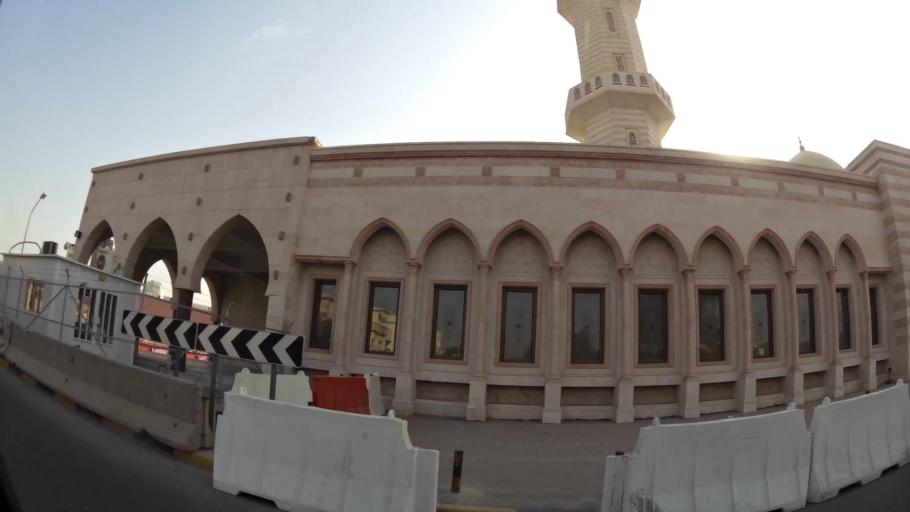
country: KW
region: Al Asimah
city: Ad Dasmah
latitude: 29.3685
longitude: 48.0000
